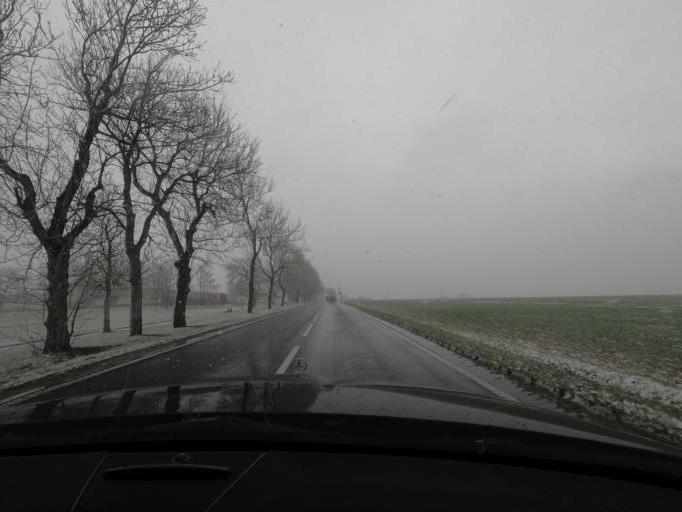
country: DE
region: Thuringia
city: Kullstedt
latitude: 51.2701
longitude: 10.2747
